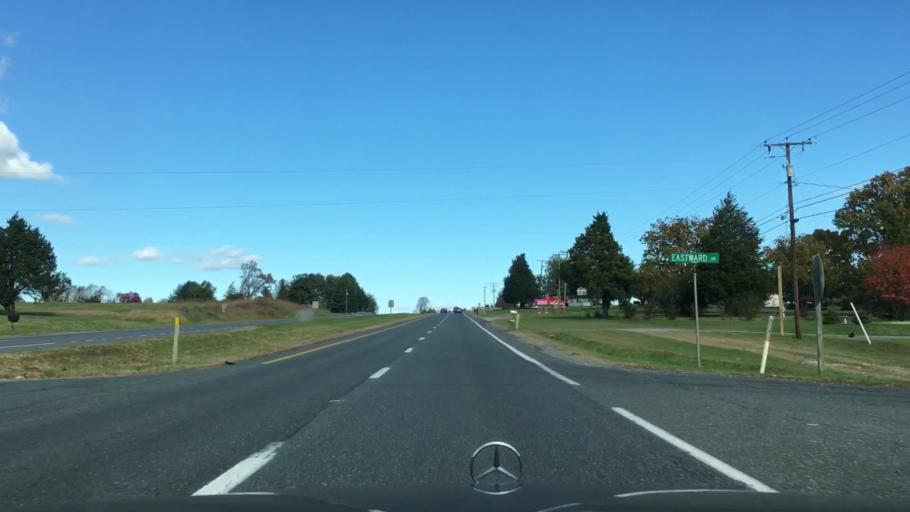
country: US
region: Virginia
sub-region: Campbell County
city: Altavista
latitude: 37.1819
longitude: -79.2046
